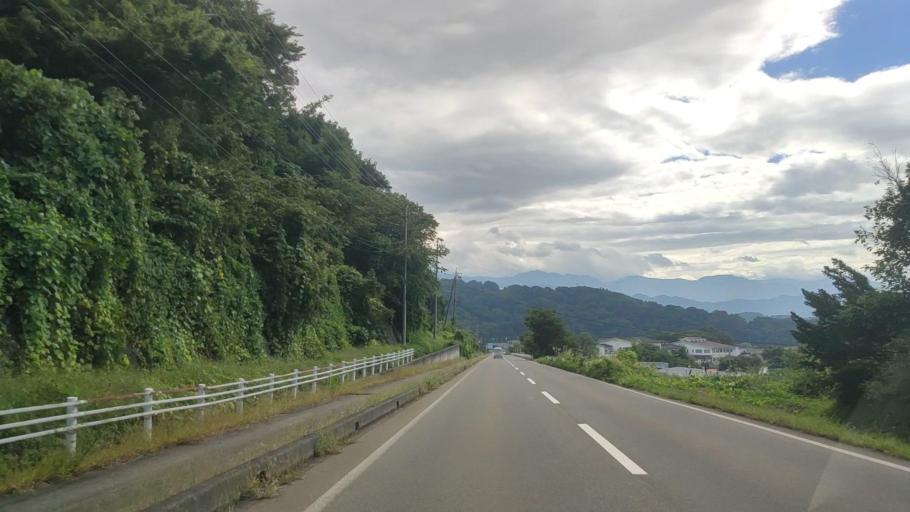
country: JP
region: Nagano
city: Nakano
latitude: 36.7773
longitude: 138.3228
